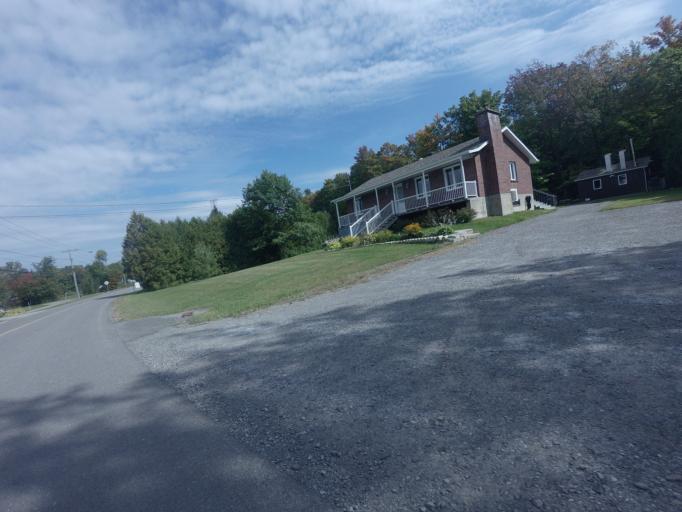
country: CA
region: Quebec
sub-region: Laurentides
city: Blainville
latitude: 45.6247
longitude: -73.9105
